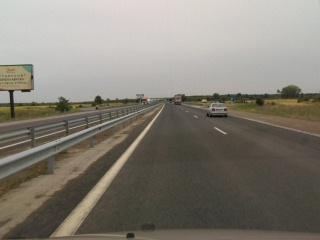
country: BG
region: Stara Zagora
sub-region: Obshtina Stara Zagora
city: Stara Zagora
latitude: 42.3277
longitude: 25.6232
